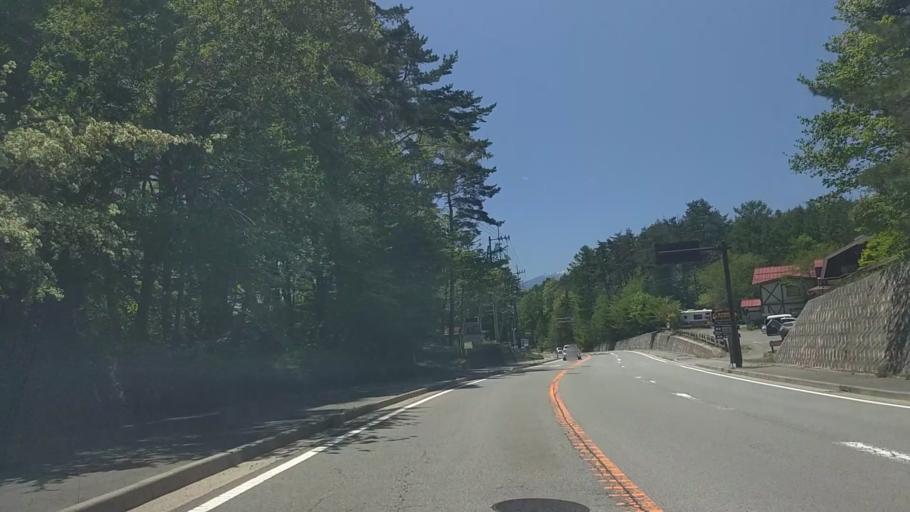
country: JP
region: Yamanashi
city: Nirasaki
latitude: 35.9020
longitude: 138.4434
